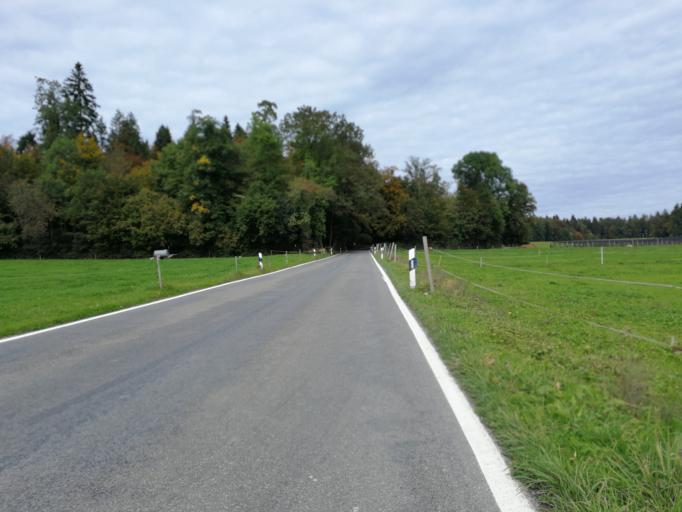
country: CH
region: Zurich
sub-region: Bezirk Meilen
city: Dorf
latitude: 47.2515
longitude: 8.7395
